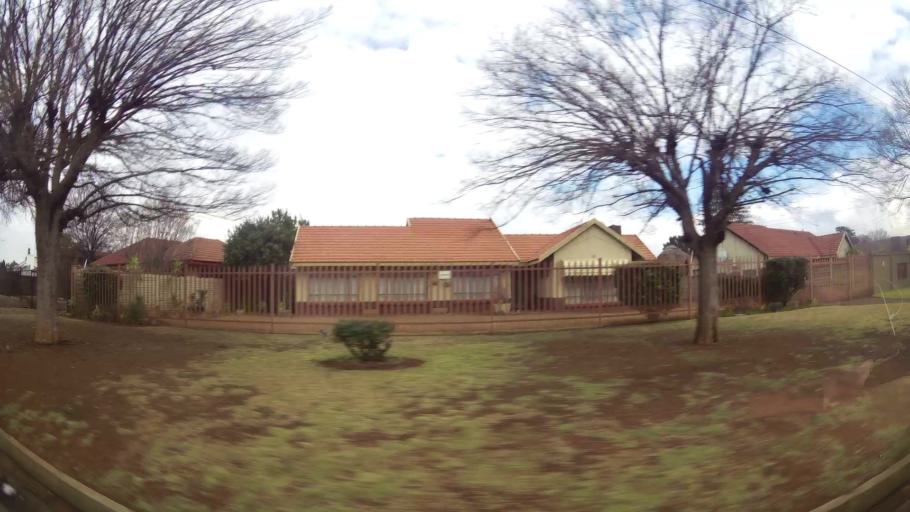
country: ZA
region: Gauteng
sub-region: Sedibeng District Municipality
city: Vereeniging
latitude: -26.6399
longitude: 27.9786
